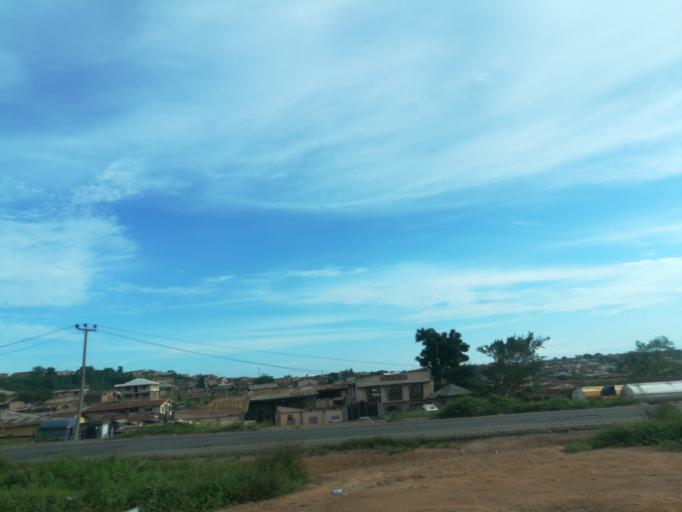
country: NG
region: Oyo
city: Ibadan
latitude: 7.3437
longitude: 3.9122
